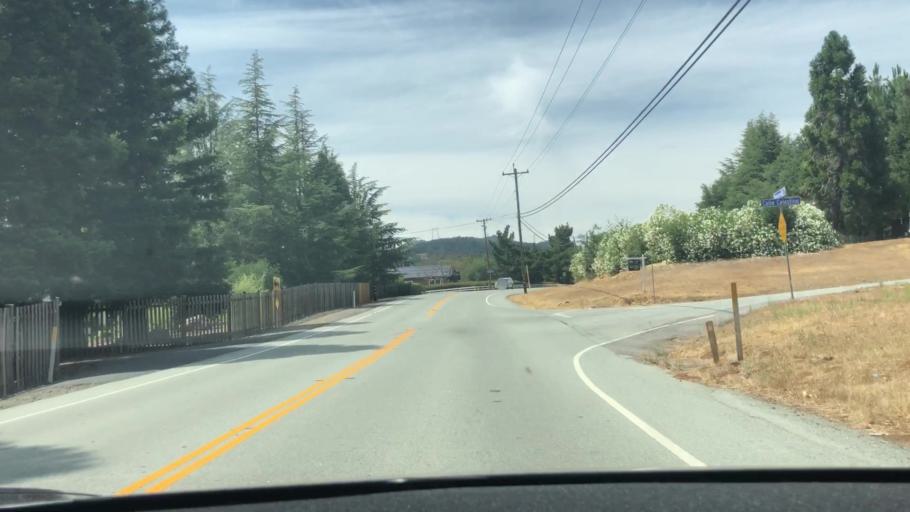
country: US
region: California
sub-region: Santa Clara County
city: San Martin
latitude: 37.0537
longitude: -121.6599
